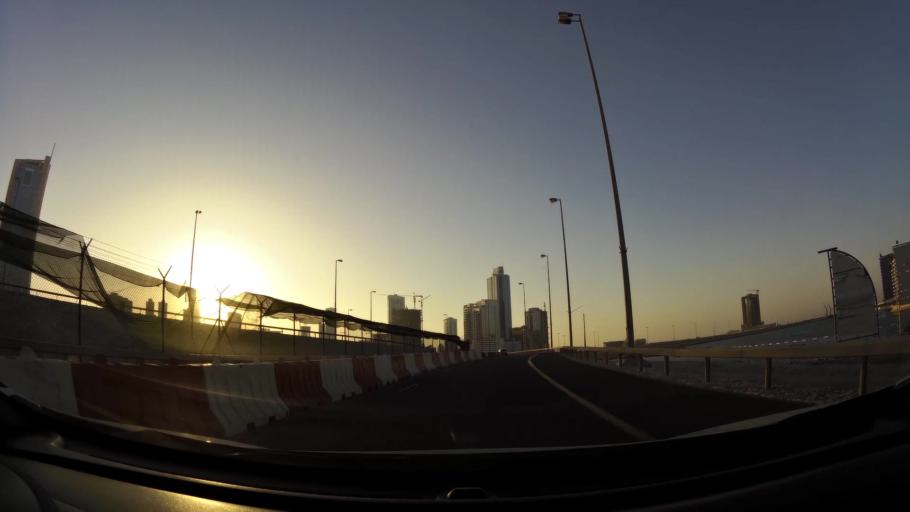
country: BH
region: Manama
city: Jidd Hafs
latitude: 26.2333
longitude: 50.5627
